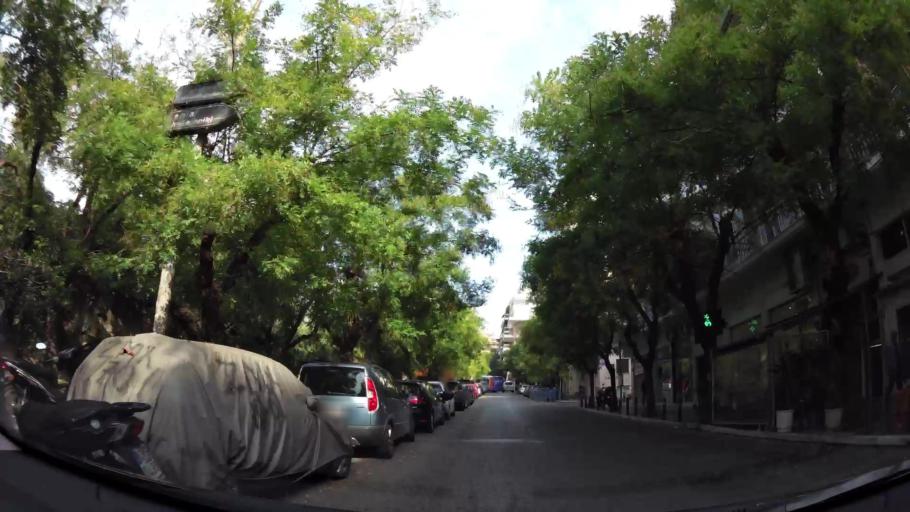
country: GR
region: Attica
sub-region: Nomarchia Athinas
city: Kipseli
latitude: 37.9901
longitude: 23.7563
